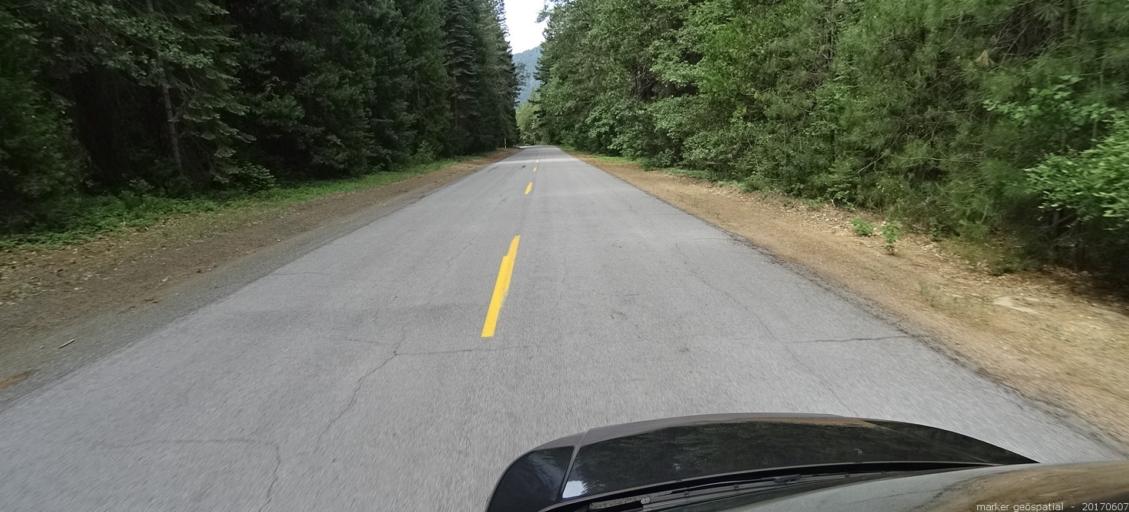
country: US
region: California
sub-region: Siskiyou County
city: Dunsmuir
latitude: 41.2455
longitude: -122.2598
